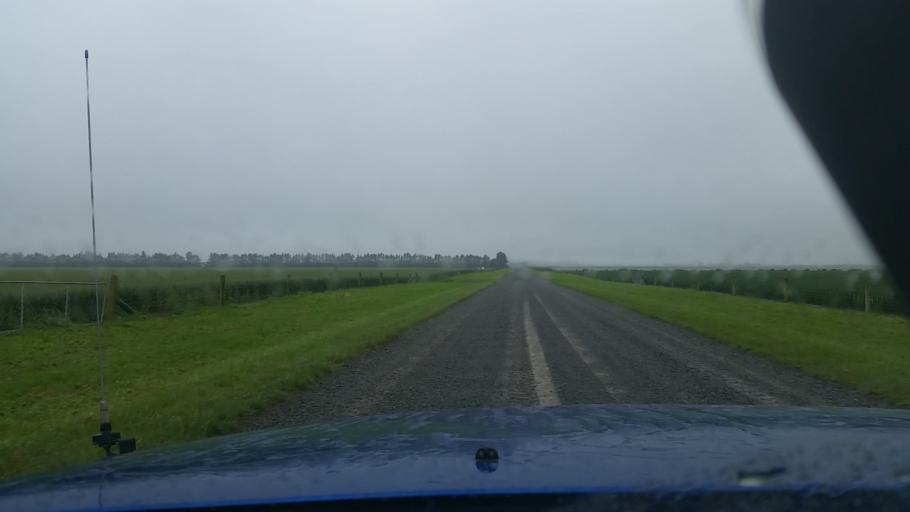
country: NZ
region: Canterbury
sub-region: Ashburton District
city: Rakaia
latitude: -43.7271
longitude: 171.8709
